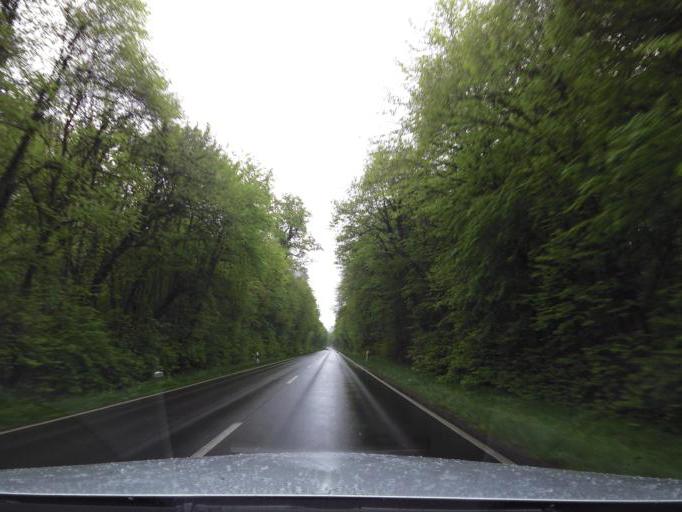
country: DE
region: Hesse
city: Morfelden-Walldorf
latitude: 49.9647
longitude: 8.5738
